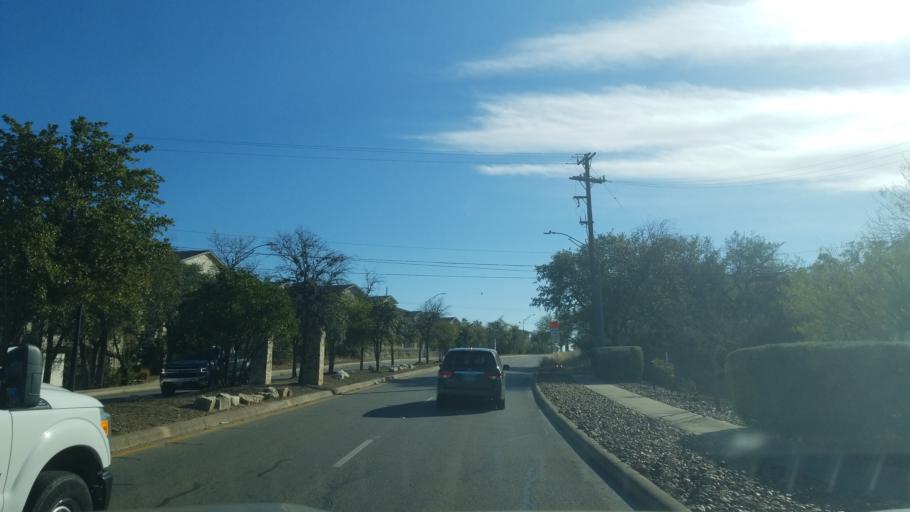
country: US
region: Texas
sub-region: Bexar County
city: Hollywood Park
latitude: 29.6206
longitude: -98.4759
